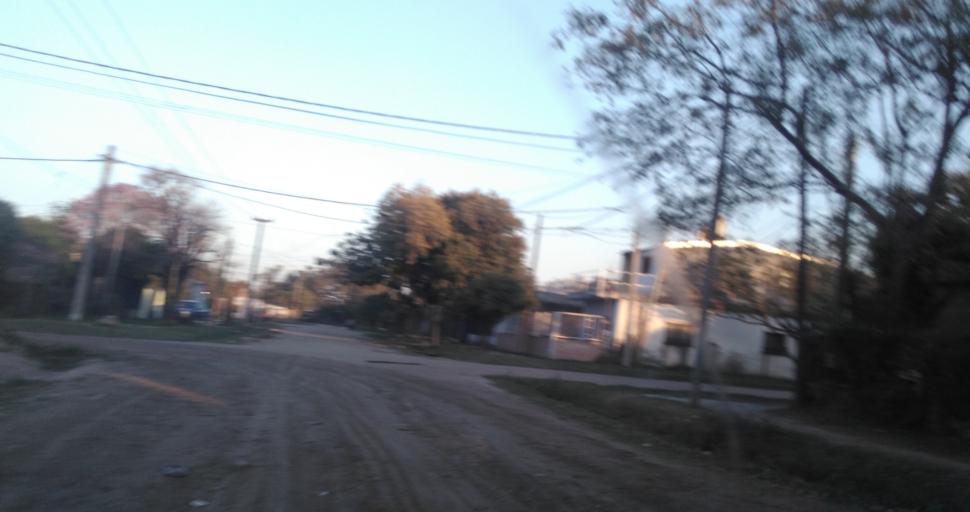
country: AR
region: Chaco
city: Fontana
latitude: -27.4275
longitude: -59.0058
